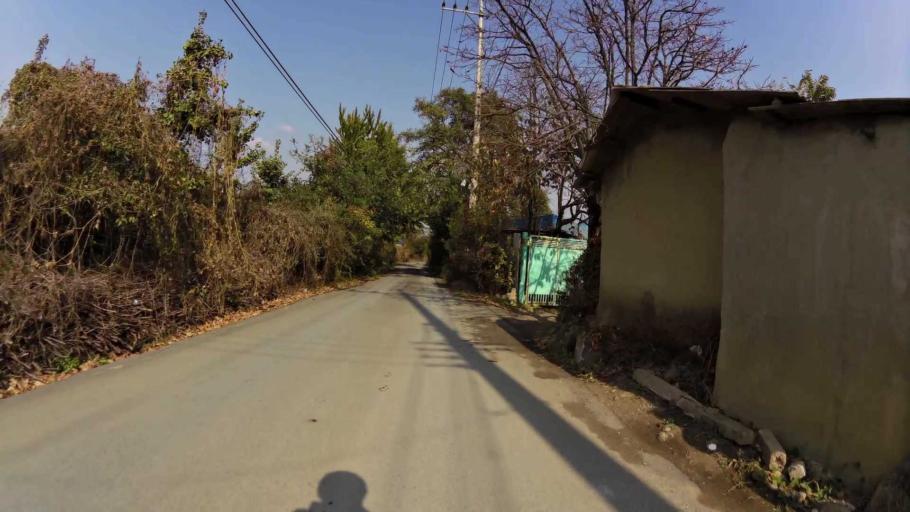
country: KR
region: Gyeongsangbuk-do
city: Gyeongsan-si
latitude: 35.8563
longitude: 128.7099
